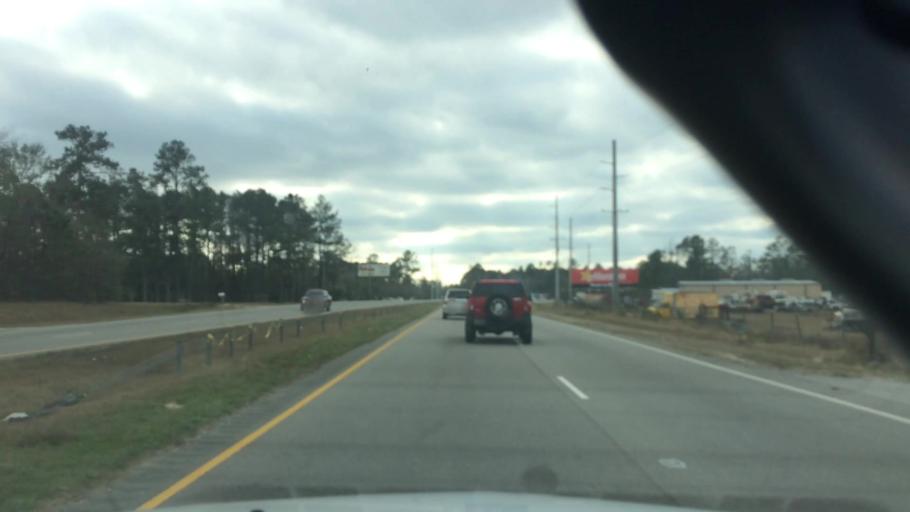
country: US
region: North Carolina
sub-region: Brunswick County
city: Bolivia
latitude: 34.0228
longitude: -78.2639
